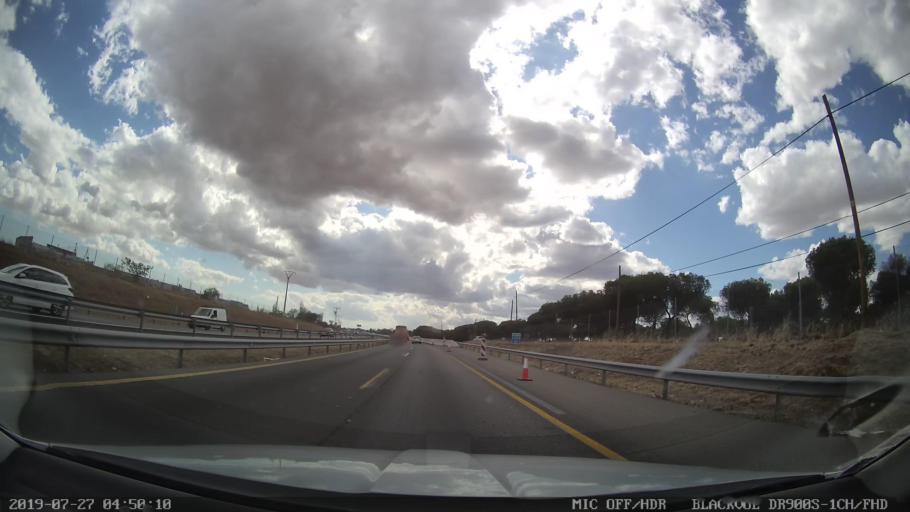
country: ES
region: Madrid
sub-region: Provincia de Madrid
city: Navalcarnero
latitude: 40.2971
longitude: -3.9640
